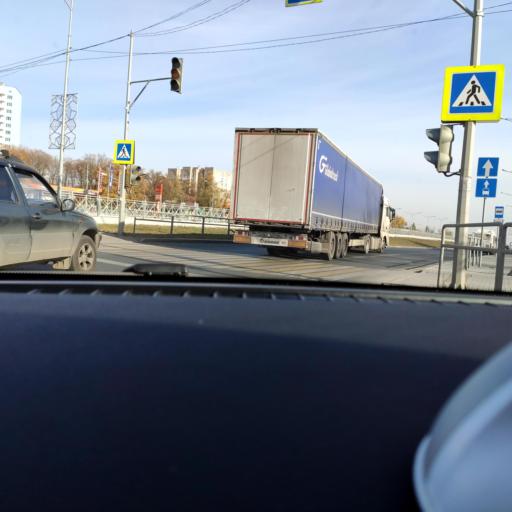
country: RU
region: Samara
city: Petra-Dubrava
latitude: 53.2747
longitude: 50.2655
